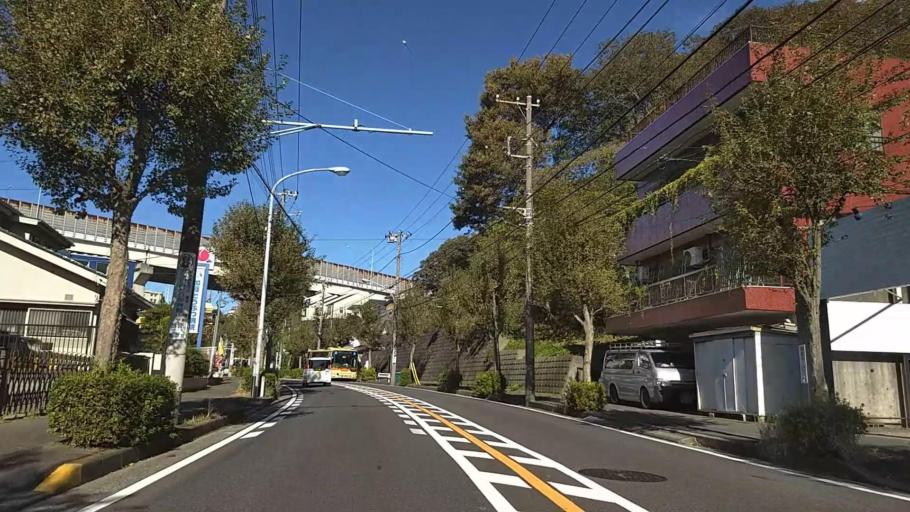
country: JP
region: Kanagawa
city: Yokohama
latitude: 35.4256
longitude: 139.5835
